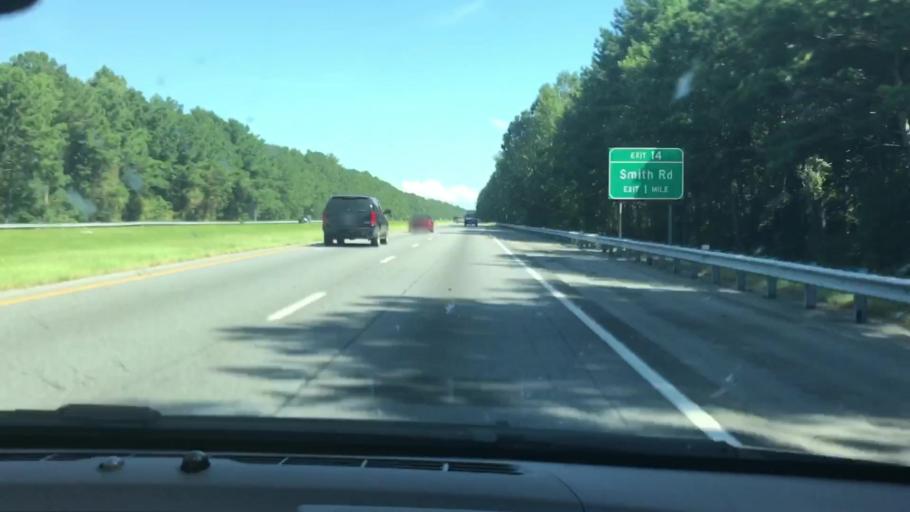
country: US
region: Alabama
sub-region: Russell County
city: Phenix City
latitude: 32.5848
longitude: -84.9600
